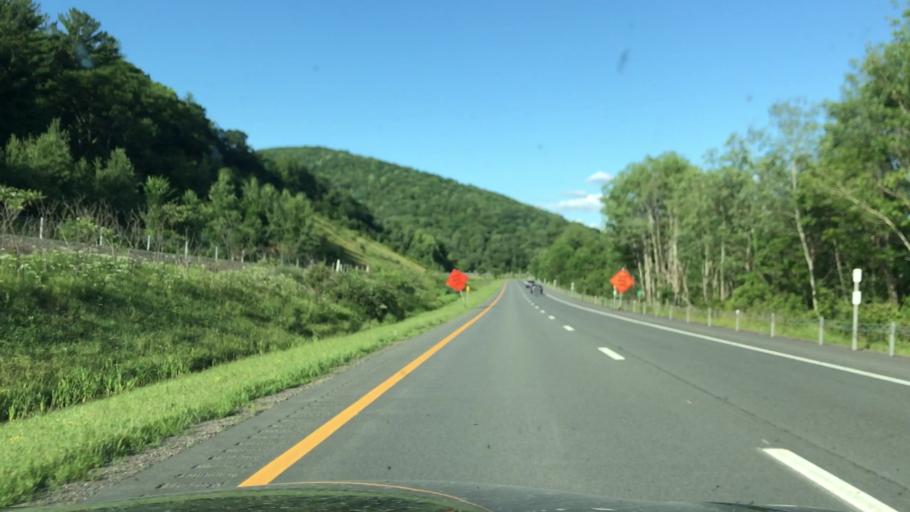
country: US
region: New York
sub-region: Delaware County
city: Hancock
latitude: 41.9823
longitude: -75.0975
